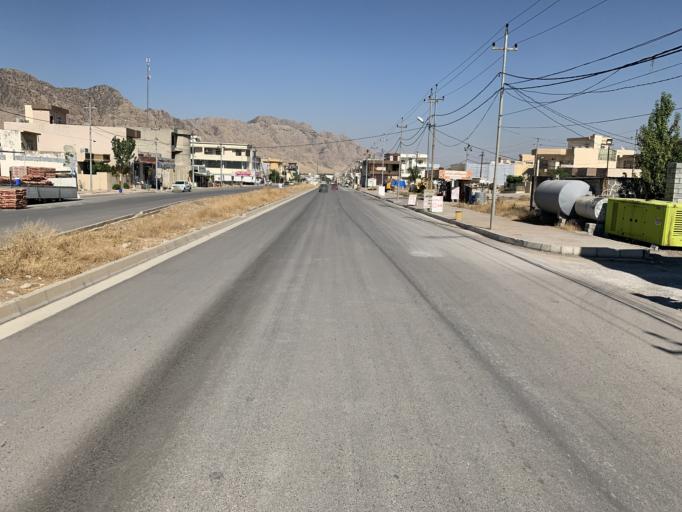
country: IQ
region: As Sulaymaniyah
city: Raniye
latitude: 36.2589
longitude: 44.8656
